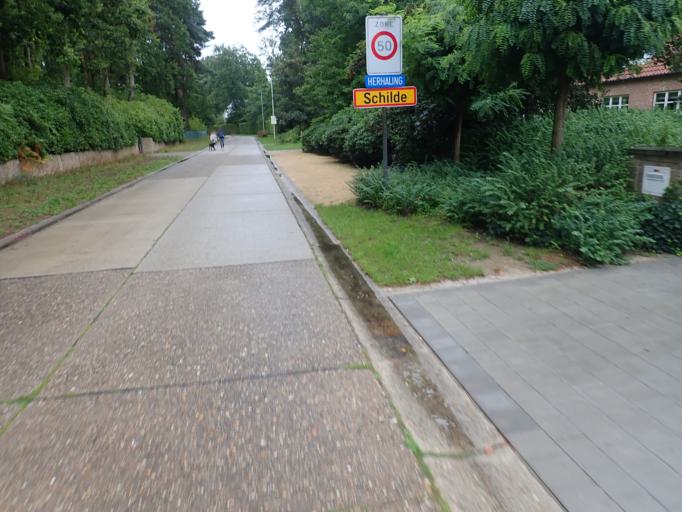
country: BE
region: Flanders
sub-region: Provincie Antwerpen
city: Wijnegem
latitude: 51.2269
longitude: 4.5508
